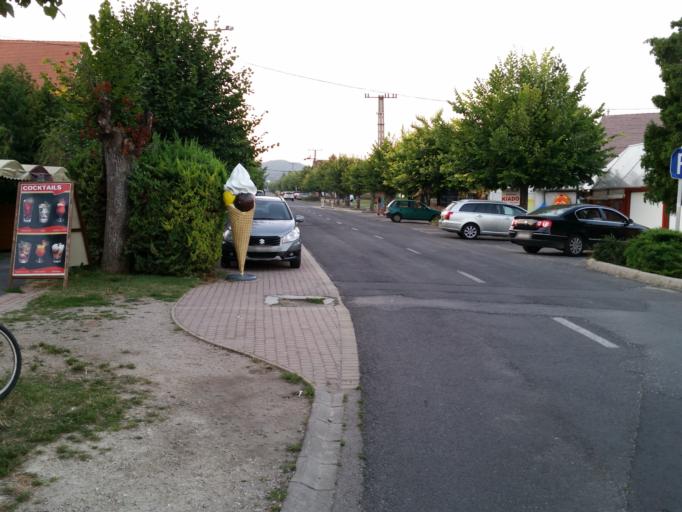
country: HU
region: Zala
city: Vonyarcvashegy
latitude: 46.7560
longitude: 17.3169
